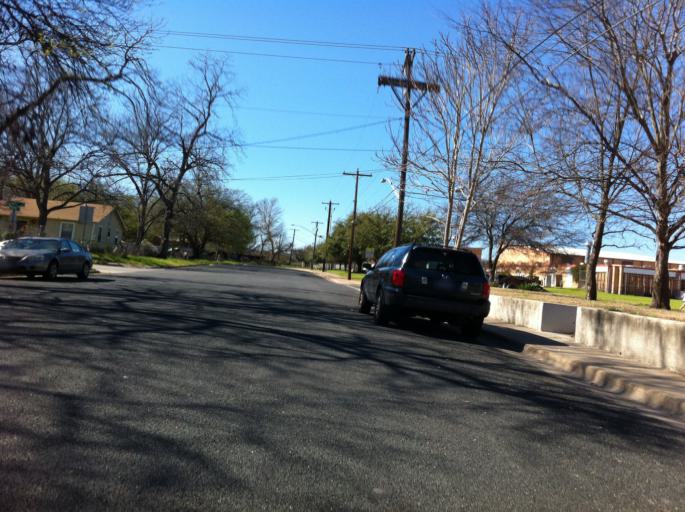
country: US
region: Texas
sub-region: Travis County
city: Austin
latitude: 30.2537
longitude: -97.7285
